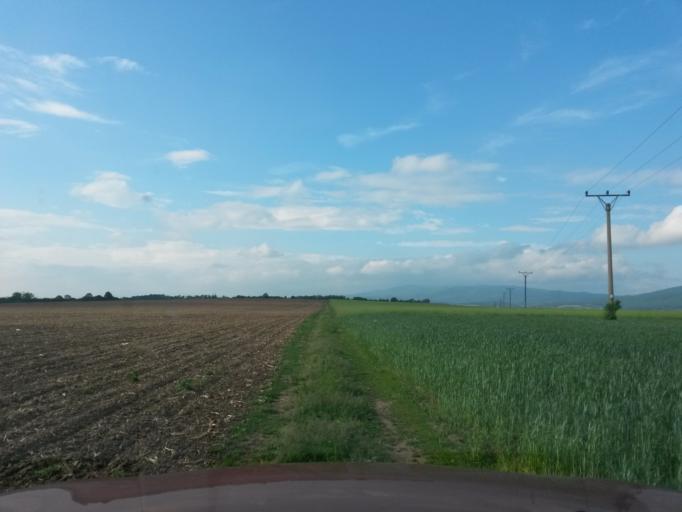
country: SK
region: Kosicky
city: Secovce
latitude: 48.7412
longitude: 21.4610
